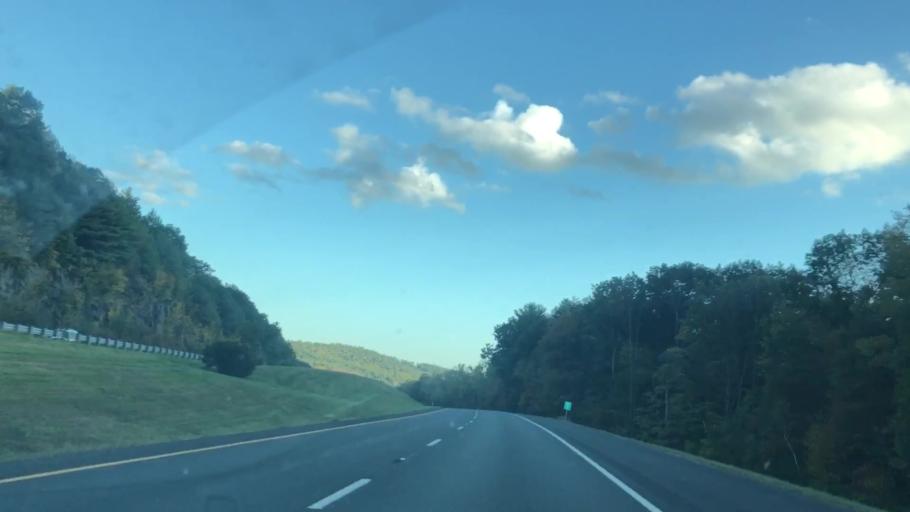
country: US
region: Massachusetts
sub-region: Franklin County
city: Bernardston
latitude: 42.7022
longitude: -72.5575
